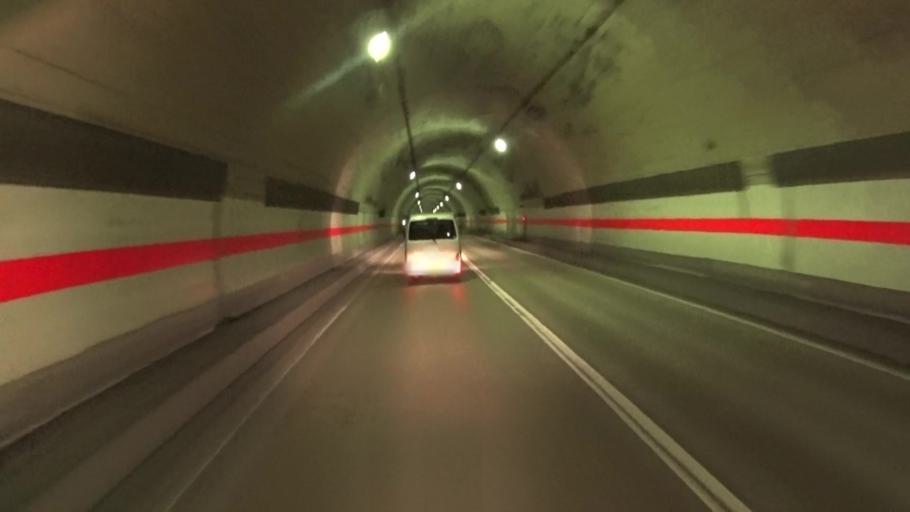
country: JP
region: Kyoto
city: Maizuru
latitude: 35.4111
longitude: 135.3347
